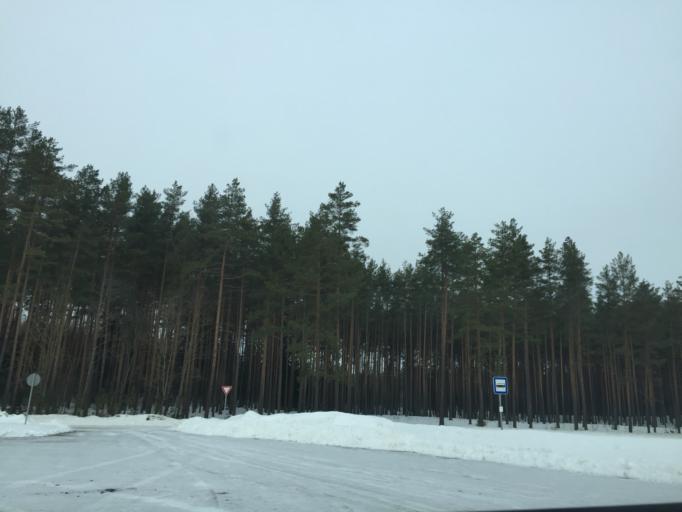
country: LV
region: Ogre
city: Ogre
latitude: 56.8414
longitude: 24.5676
